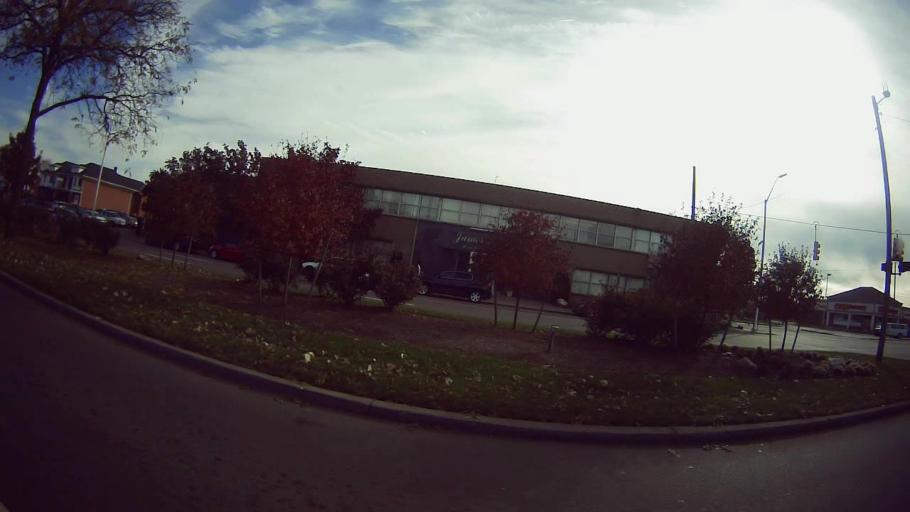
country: US
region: Michigan
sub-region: Wayne County
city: Highland Park
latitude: 42.3642
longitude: -83.0897
